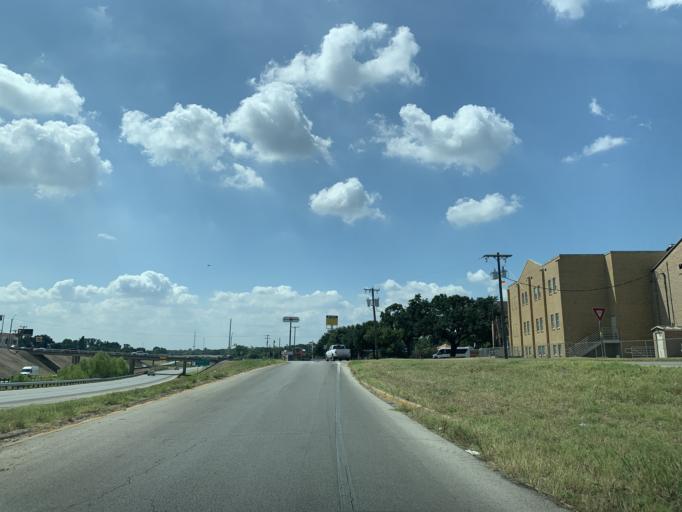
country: US
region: Texas
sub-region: Tarrant County
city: Azle
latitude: 32.8938
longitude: -97.5415
